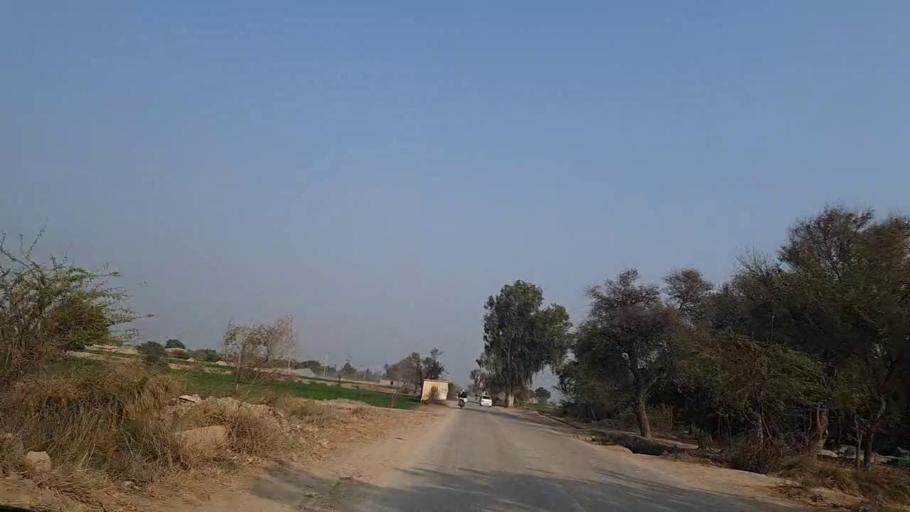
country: PK
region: Sindh
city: Sakrand
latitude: 26.1320
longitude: 68.2272
